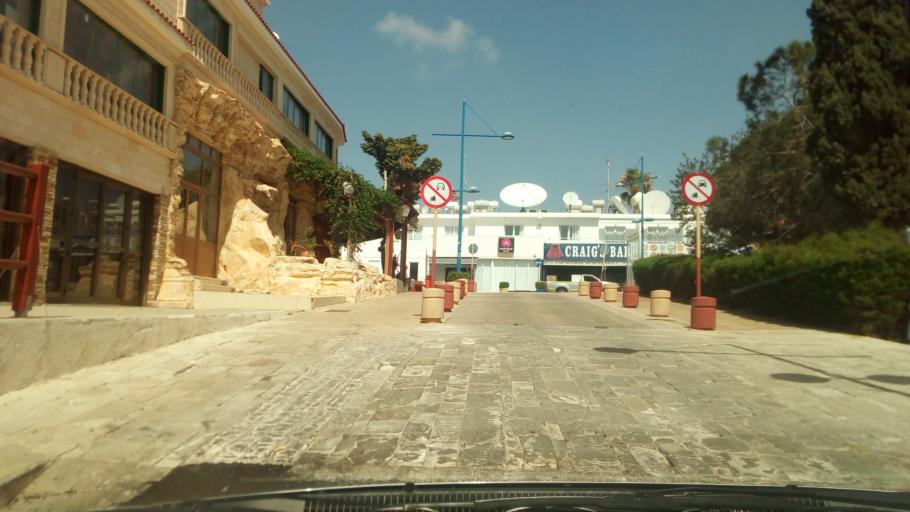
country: CY
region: Ammochostos
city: Ayia Napa
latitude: 34.9894
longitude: 33.9937
